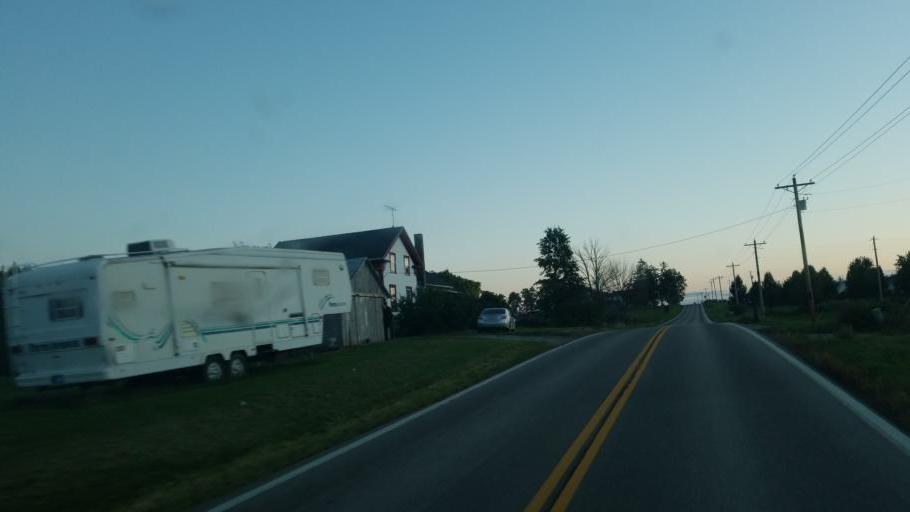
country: US
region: Ohio
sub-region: Ashland County
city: Ashland
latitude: 40.9210
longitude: -82.4012
